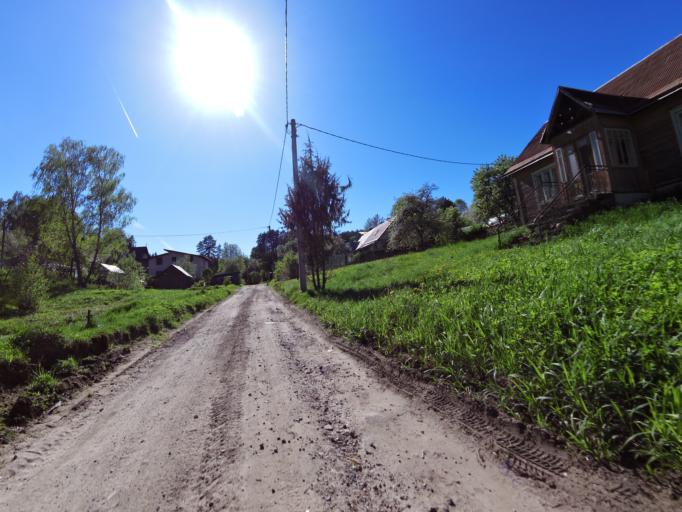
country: LT
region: Vilnius County
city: Pilaite
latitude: 54.6862
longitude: 25.1538
